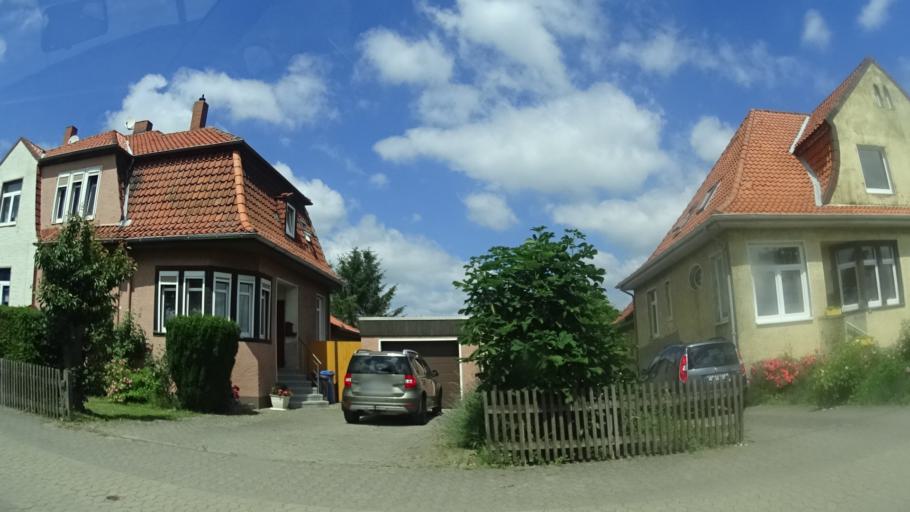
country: DE
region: Lower Saxony
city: Hildesheim
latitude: 52.1613
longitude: 10.0097
